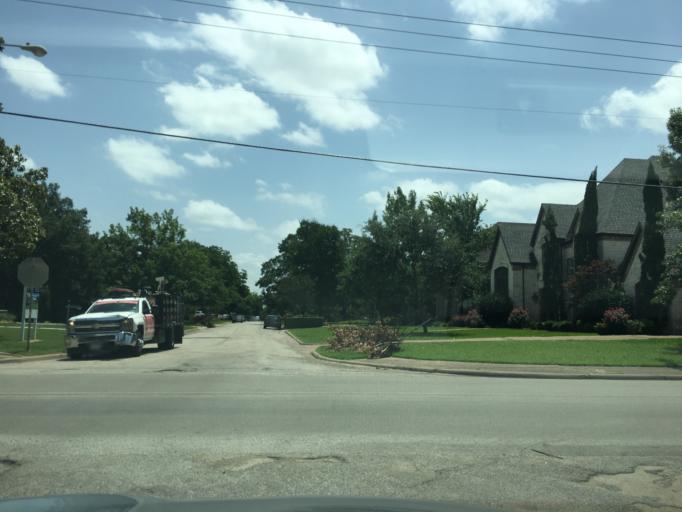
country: US
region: Texas
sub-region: Dallas County
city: University Park
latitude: 32.8937
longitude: -96.7933
